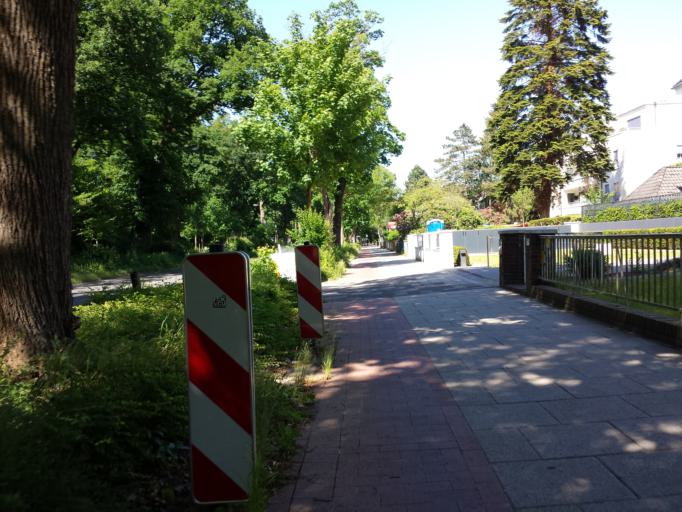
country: DE
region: Bremen
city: Bremen
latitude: 53.0977
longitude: 8.8359
